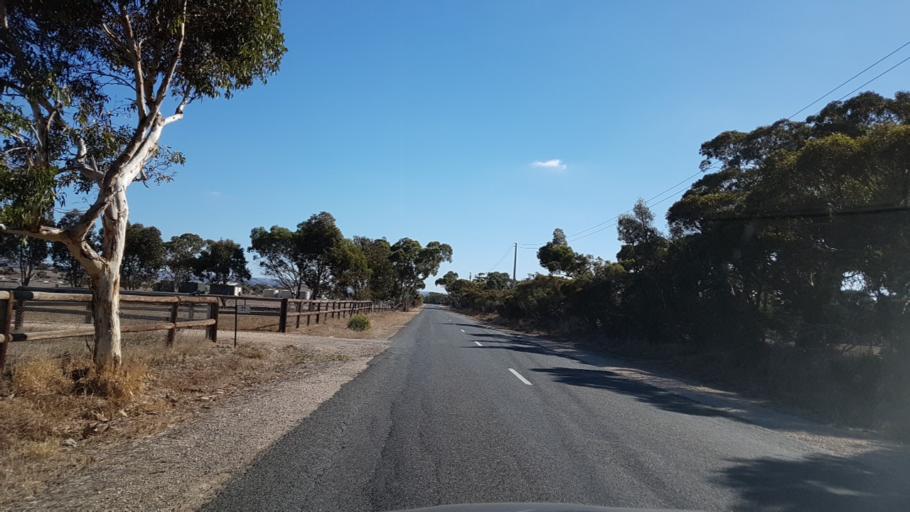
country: AU
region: South Australia
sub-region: Alexandrina
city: Goolwa
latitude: -35.3767
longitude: 138.8197
